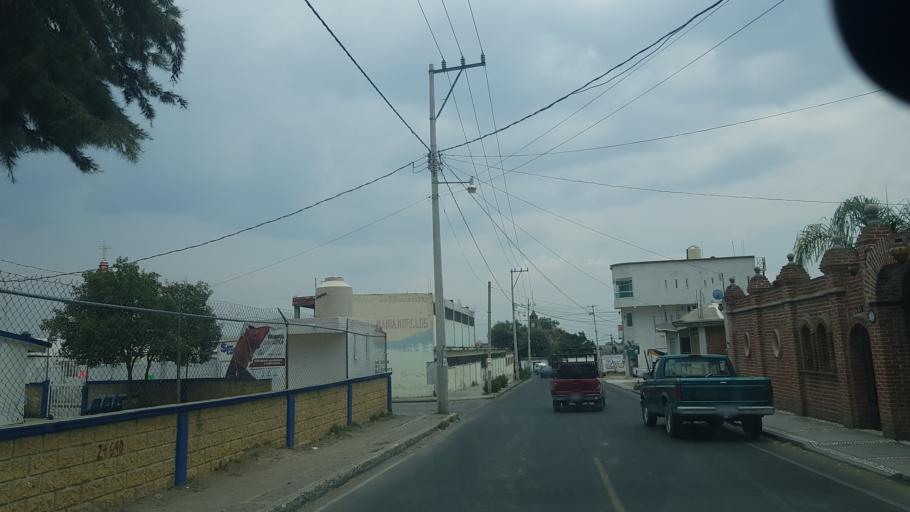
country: MX
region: Puebla
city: San Lorenzo Chiautzingo
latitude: 19.1976
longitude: -98.4414
